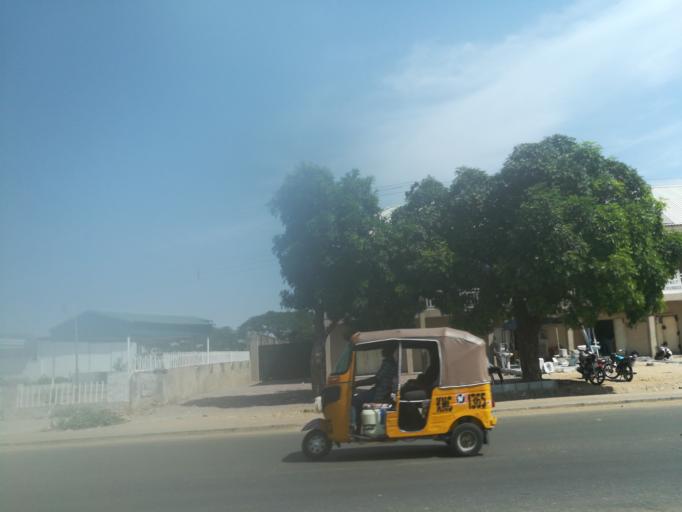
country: NG
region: Kano
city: Kano
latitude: 12.0217
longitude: 8.5172
